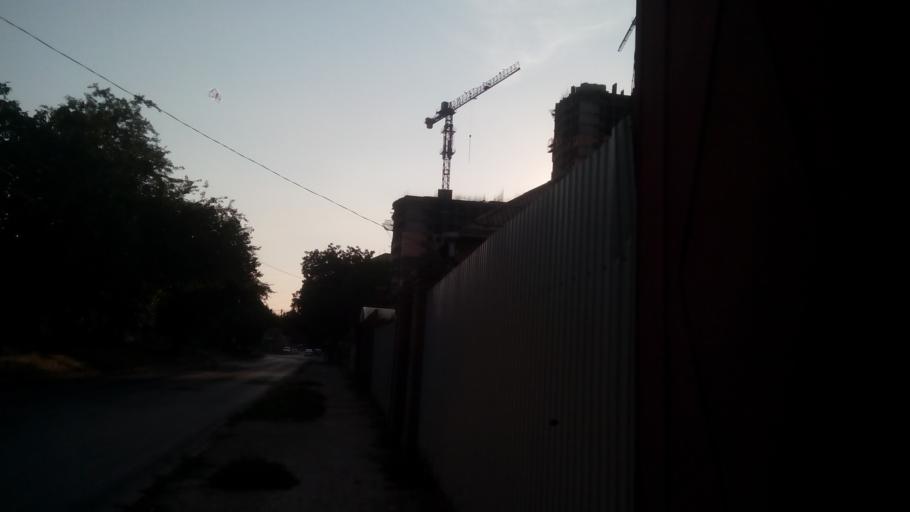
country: RU
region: Rostov
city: Imeni Chkalova
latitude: 47.2565
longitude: 39.7762
